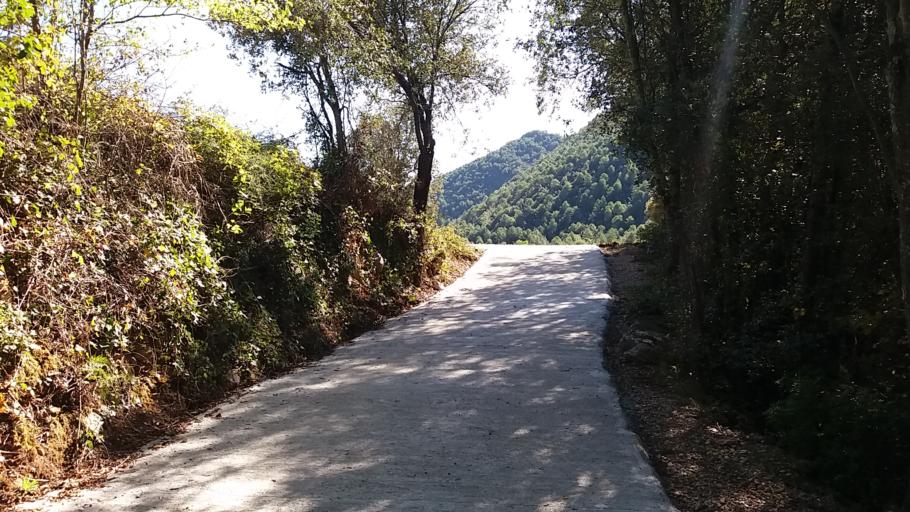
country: ES
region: Catalonia
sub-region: Provincia de Girona
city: Sant Llorenc de la Muga
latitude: 42.3049
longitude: 2.7246
